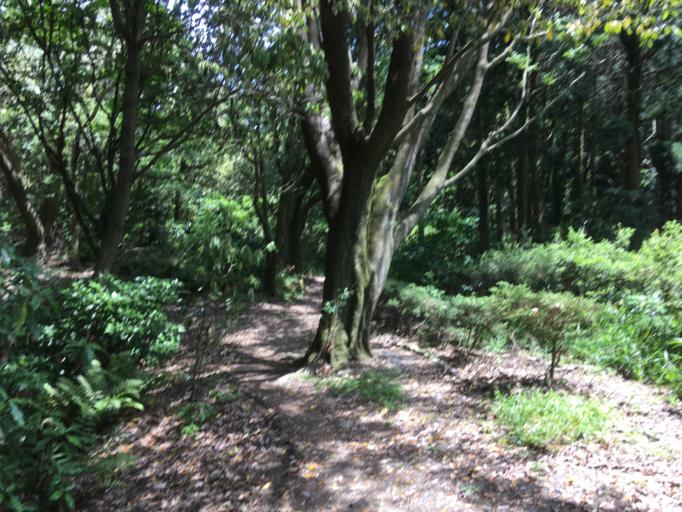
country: JP
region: Nara
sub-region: Ikoma-shi
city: Ikoma
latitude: 34.6657
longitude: 135.6662
